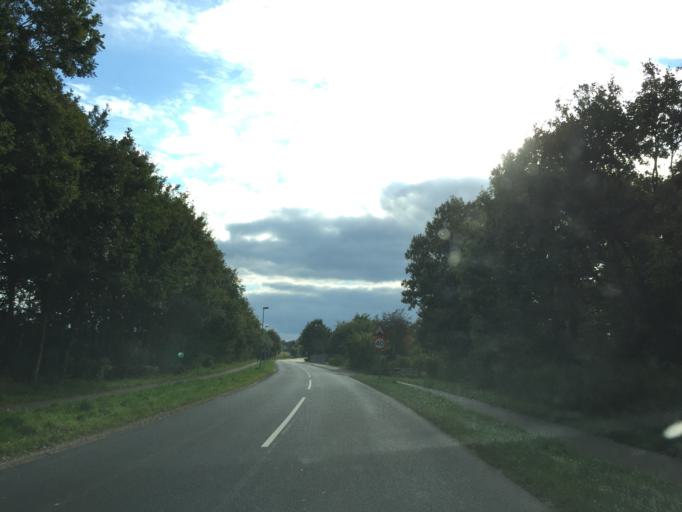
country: DK
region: Central Jutland
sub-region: Viborg Kommune
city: Bjerringbro
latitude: 56.2750
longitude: 9.7332
